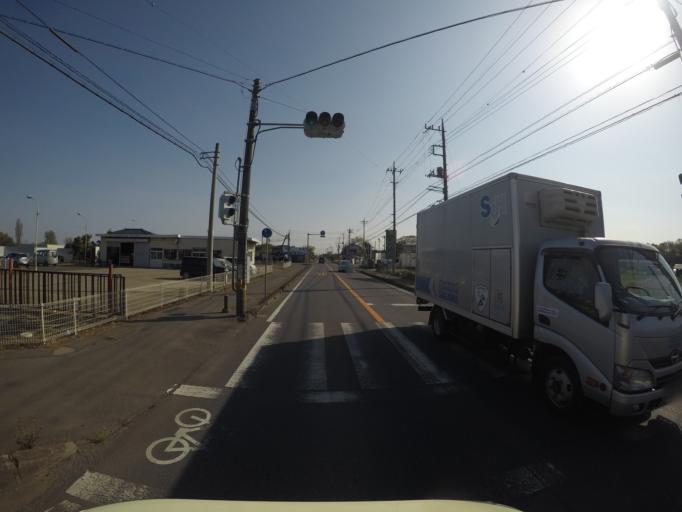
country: JP
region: Ibaraki
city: Yuki
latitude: 36.2581
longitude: 139.8734
